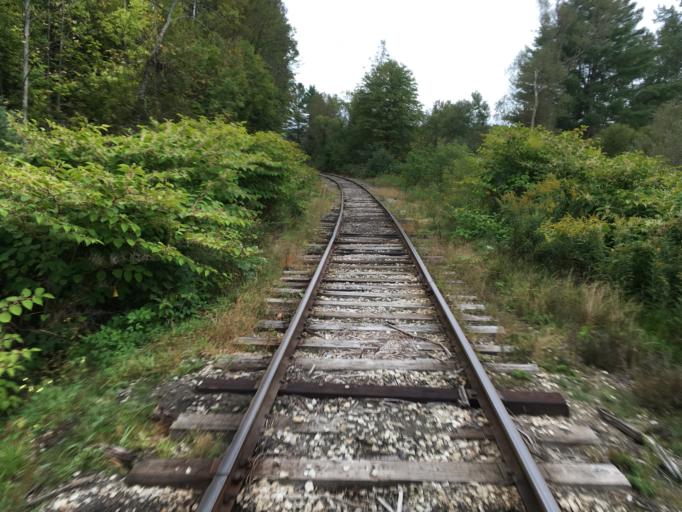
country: US
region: Vermont
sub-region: Washington County
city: Montpelier
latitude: 44.2361
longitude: -72.5502
